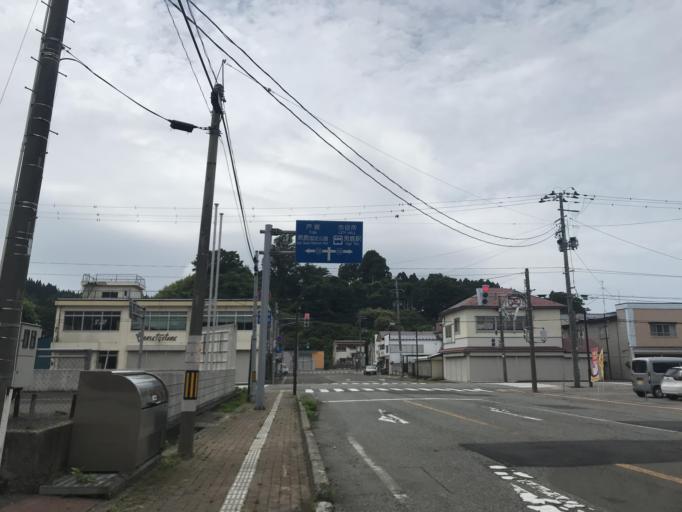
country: JP
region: Akita
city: Tenno
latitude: 39.8827
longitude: 139.8471
